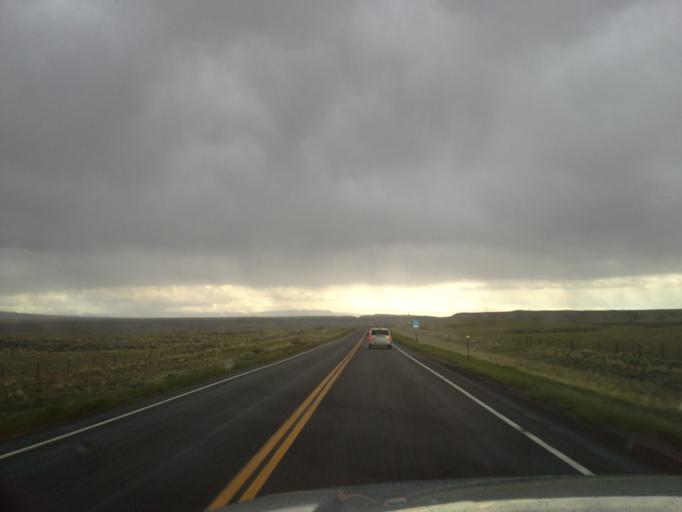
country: US
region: Wyoming
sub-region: Park County
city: Powell
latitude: 45.0718
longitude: -108.6849
